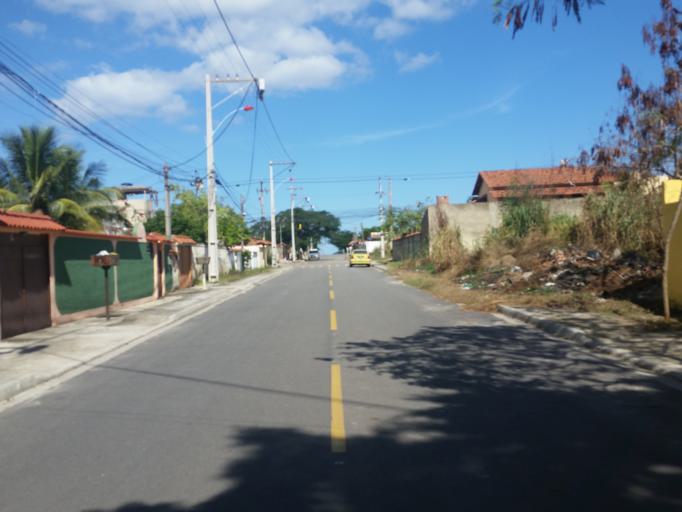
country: BR
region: Rio de Janeiro
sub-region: Marica
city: Marica
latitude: -22.9640
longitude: -42.9667
